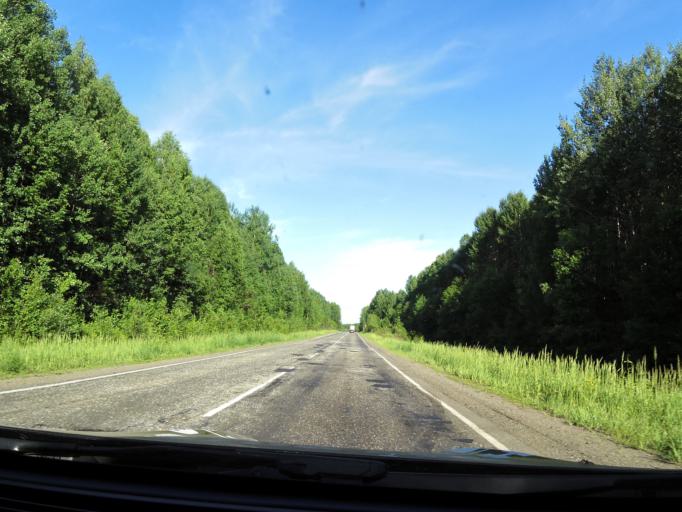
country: RU
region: Kirov
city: Chernaya Kholunitsa
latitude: 58.8785
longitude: 51.4568
